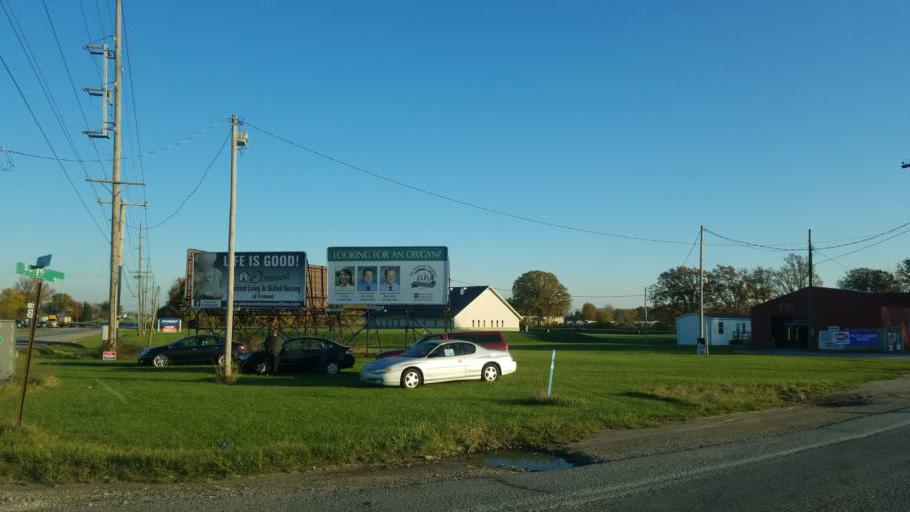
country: US
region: Ohio
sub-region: Sandusky County
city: Fremont
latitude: 41.3306
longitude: -83.0517
